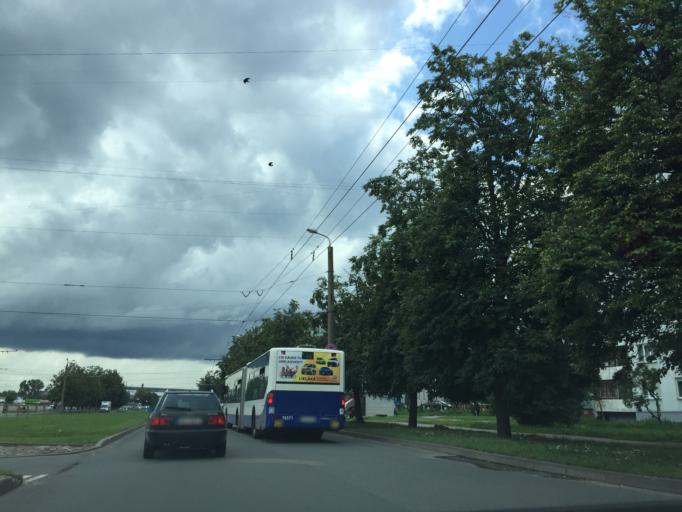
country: LV
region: Stopini
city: Ulbroka
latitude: 56.9348
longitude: 24.2018
